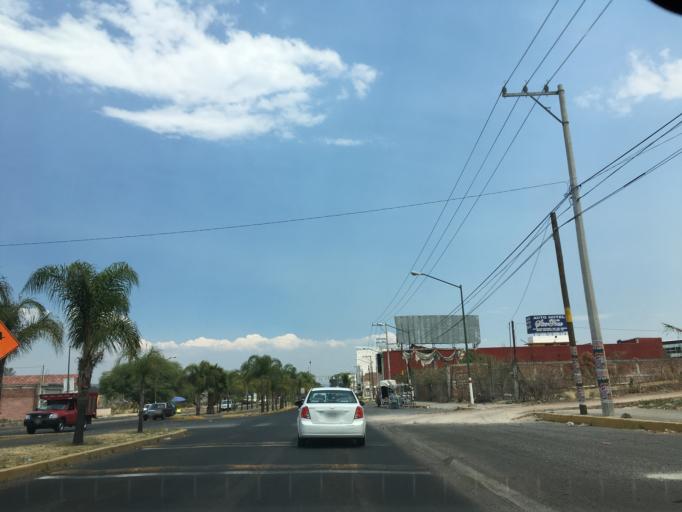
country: MX
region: Guanajuato
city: Moroleon
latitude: 20.1042
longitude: -101.1661
